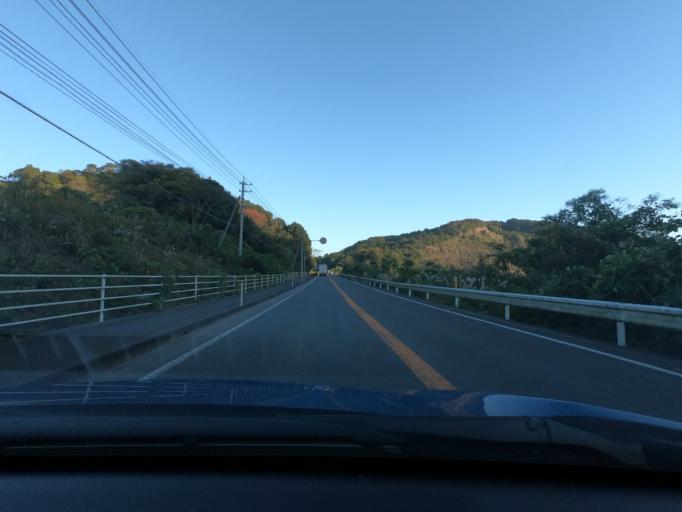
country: JP
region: Kagoshima
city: Satsumasendai
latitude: 31.8460
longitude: 130.2730
